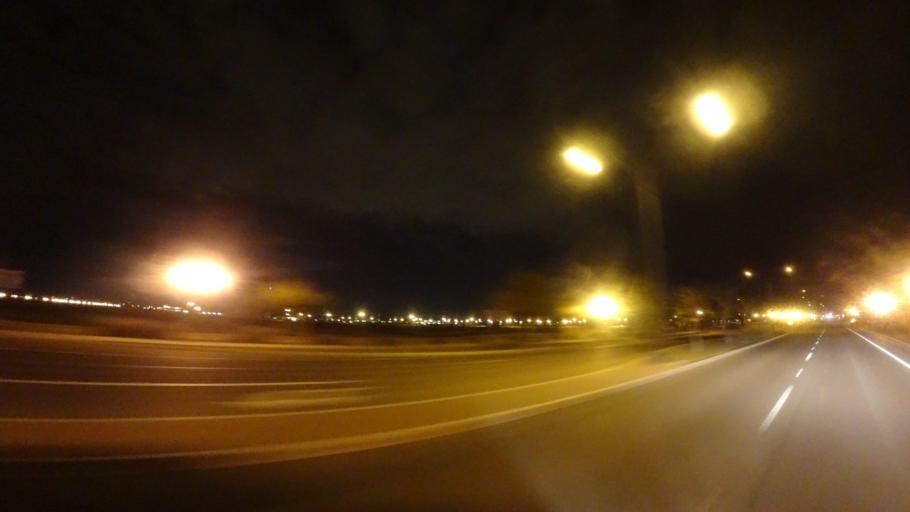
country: US
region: Arizona
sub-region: Maricopa County
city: Queen Creek
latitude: 33.3093
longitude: -111.7038
